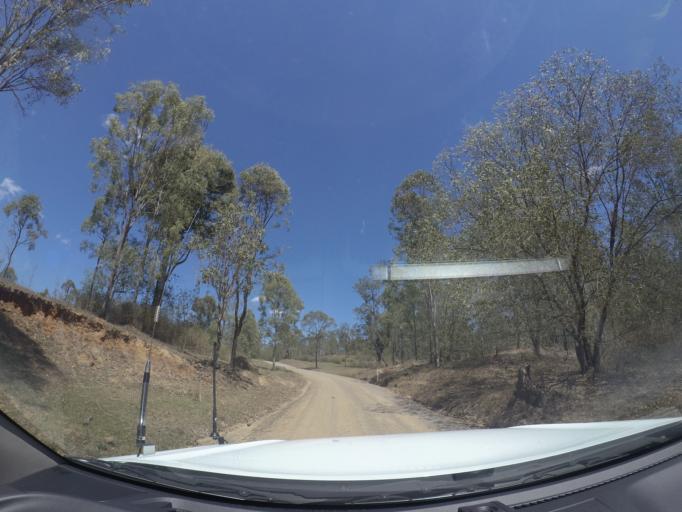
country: AU
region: Queensland
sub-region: Logan
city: Cedar Vale
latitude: -27.8651
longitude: 152.8494
